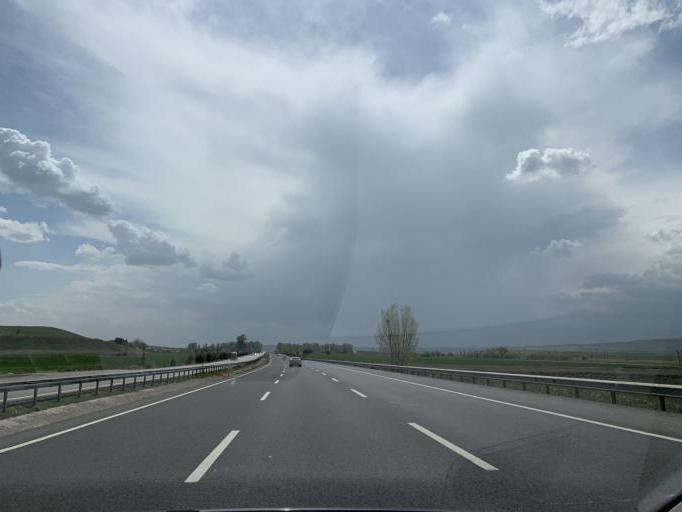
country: TR
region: Ankara
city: Temelli
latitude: 39.7002
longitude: 32.2681
